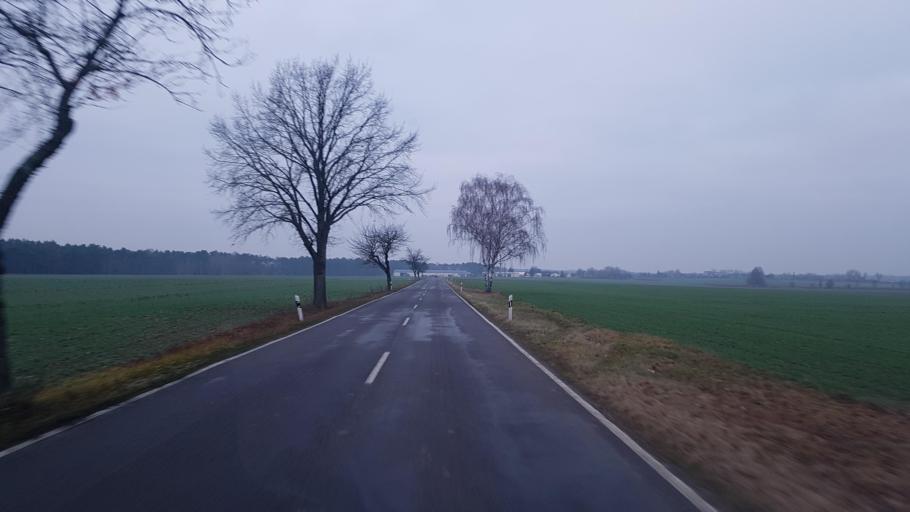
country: DE
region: Brandenburg
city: Ruckersdorf
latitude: 51.5553
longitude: 13.6168
